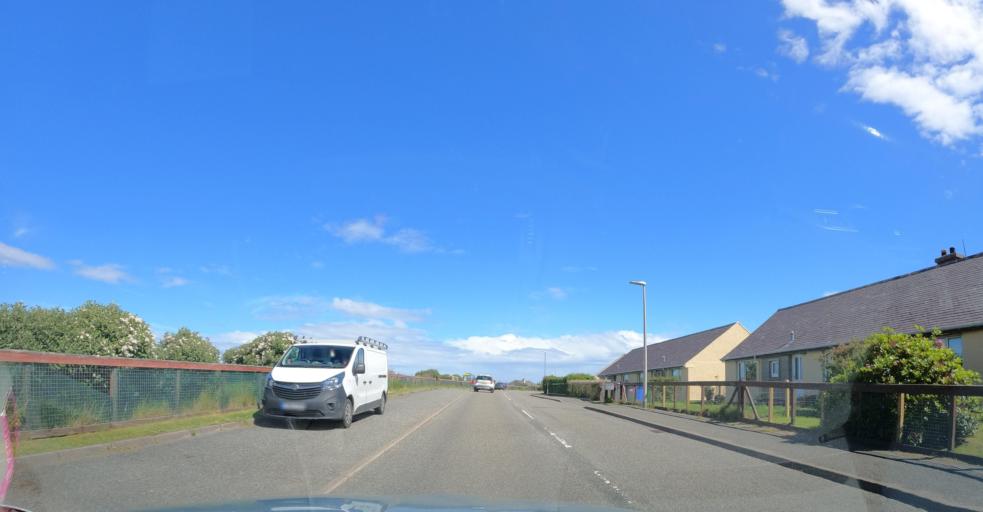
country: GB
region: Scotland
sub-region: Eilean Siar
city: Isle of Lewis
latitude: 58.2477
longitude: -6.3977
